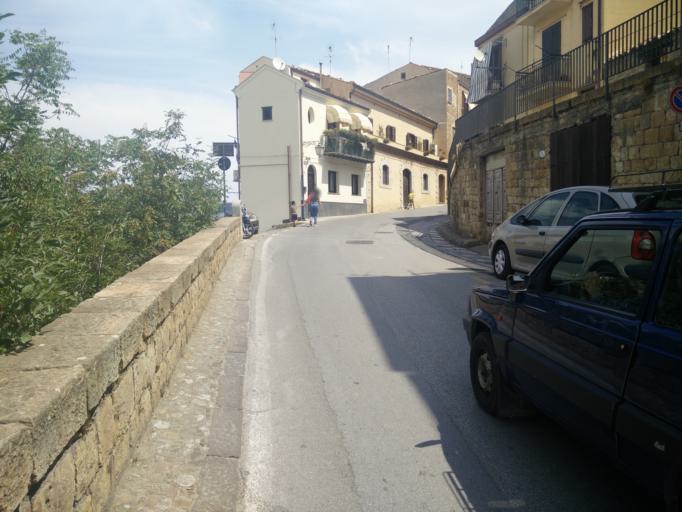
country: IT
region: Sicily
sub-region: Palermo
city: Castelbuono
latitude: 37.9303
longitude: 14.0857
